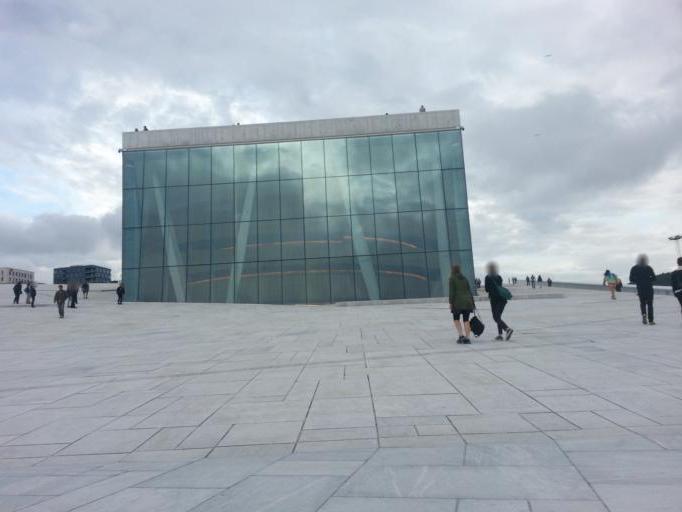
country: NO
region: Oslo
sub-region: Oslo
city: Oslo
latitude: 59.9075
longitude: 10.7510
